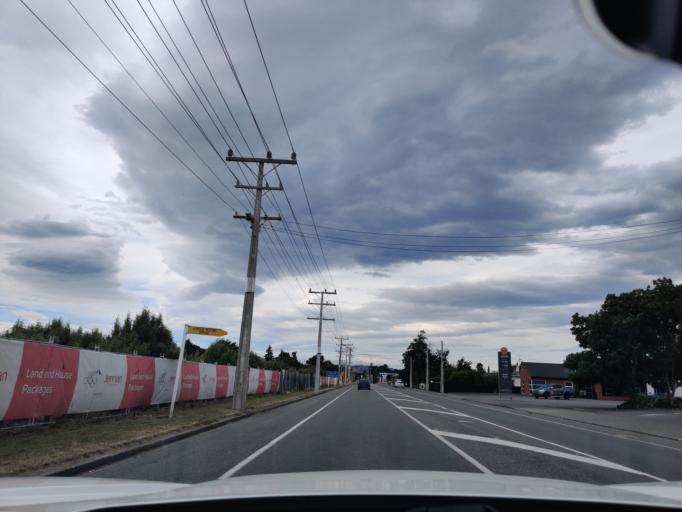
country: NZ
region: Wellington
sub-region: Masterton District
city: Masterton
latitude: -40.9476
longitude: 175.6355
